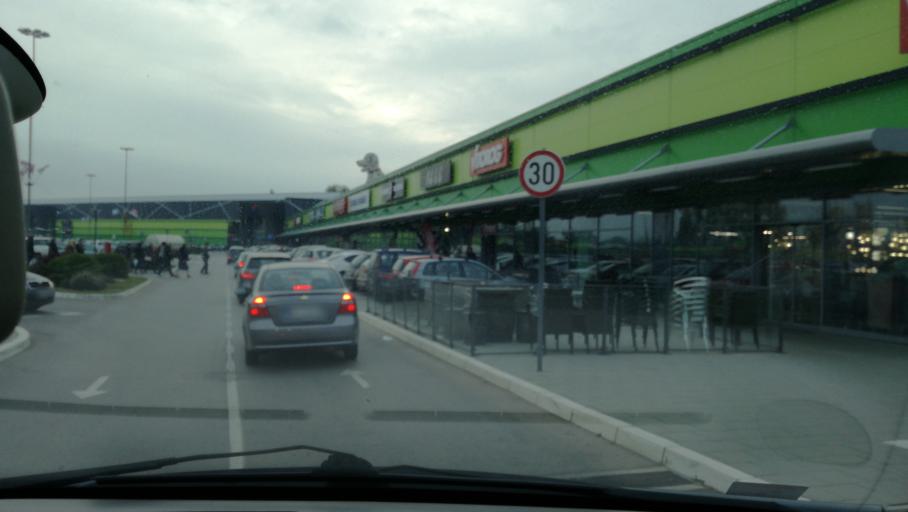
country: RS
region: Autonomna Pokrajina Vojvodina
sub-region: Juznobacki Okrug
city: Novi Sad
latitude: 45.2777
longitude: 19.8278
